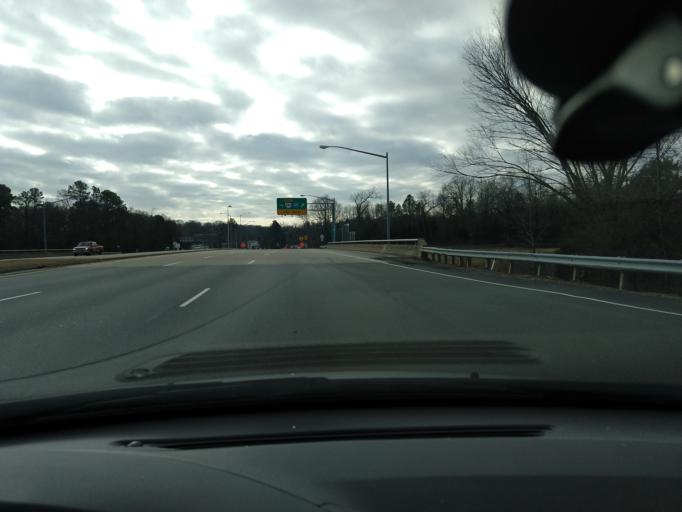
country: US
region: Virginia
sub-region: Chesterfield County
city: Bensley
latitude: 37.4442
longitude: -77.4404
